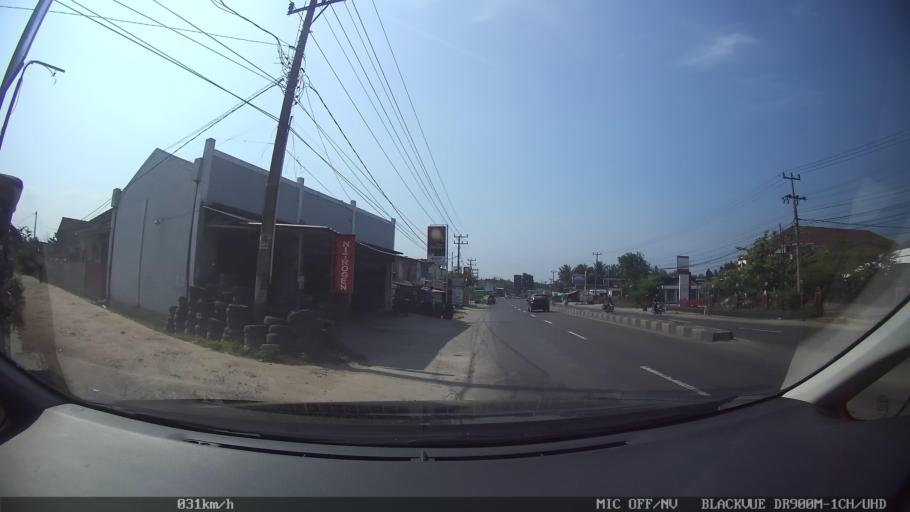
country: ID
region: Lampung
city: Natar
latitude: -5.2570
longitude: 105.1840
